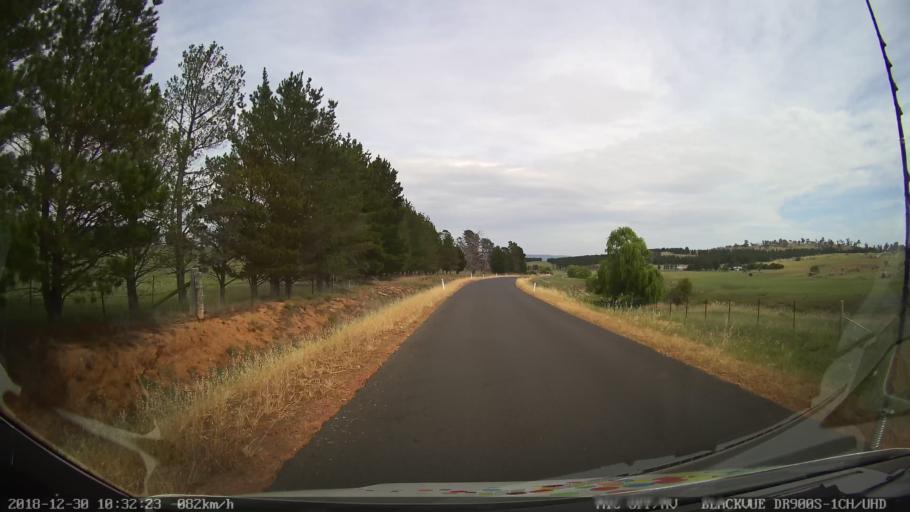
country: AU
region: New South Wales
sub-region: Snowy River
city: Berridale
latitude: -36.5010
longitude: 148.8670
